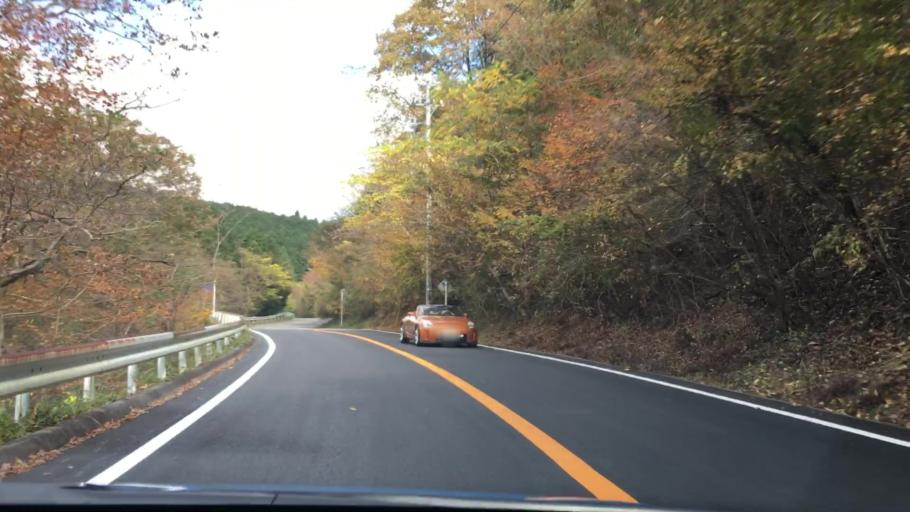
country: JP
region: Shizuoka
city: Gotemba
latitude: 35.3836
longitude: 138.9434
